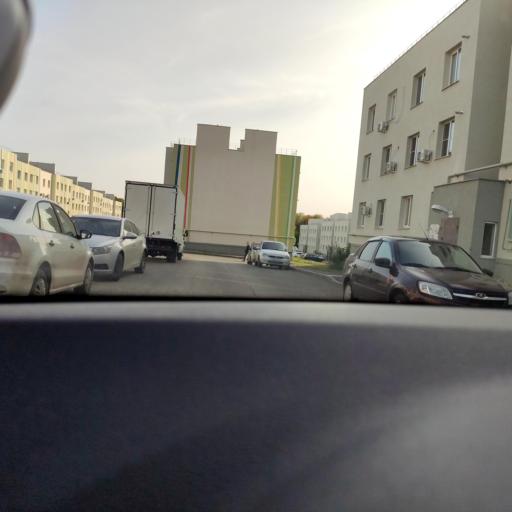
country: RU
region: Samara
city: Petra-Dubrava
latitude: 53.3026
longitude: 50.3432
